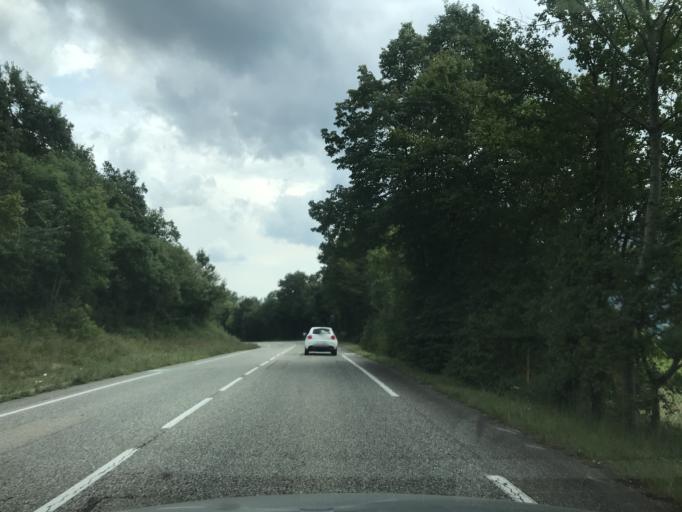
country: FR
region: Rhone-Alpes
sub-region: Departement de la Savoie
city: Chatillon
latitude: 45.7875
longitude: 5.8609
